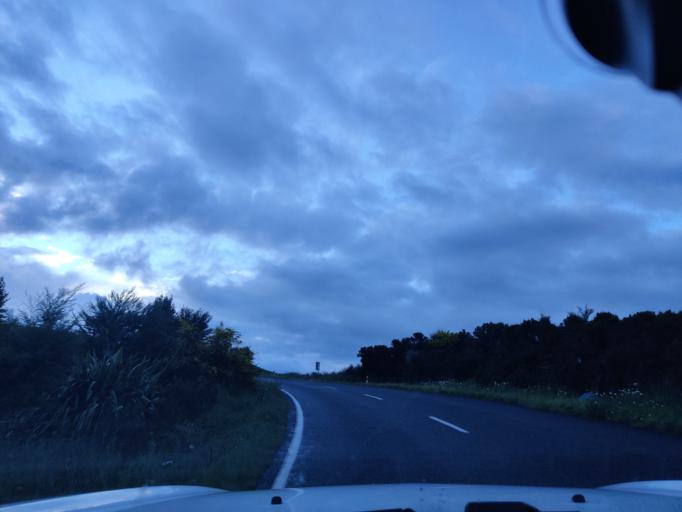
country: NZ
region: Waikato
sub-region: South Waikato District
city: Tokoroa
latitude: -38.2036
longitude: 175.8126
